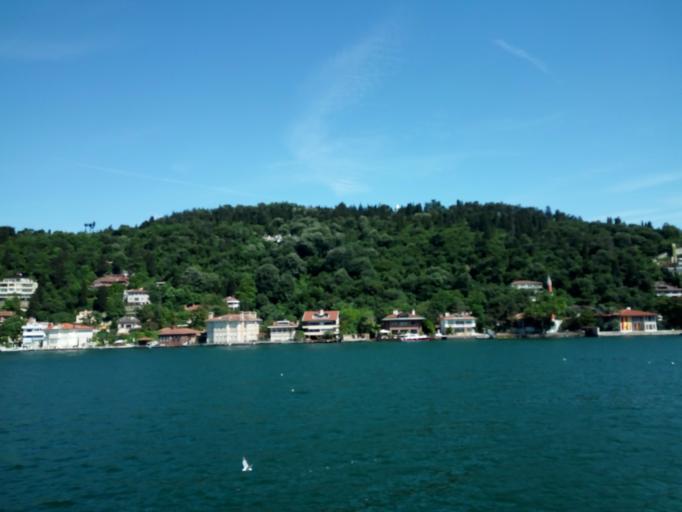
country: TR
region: Istanbul
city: UEskuedar
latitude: 41.0661
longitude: 29.0531
